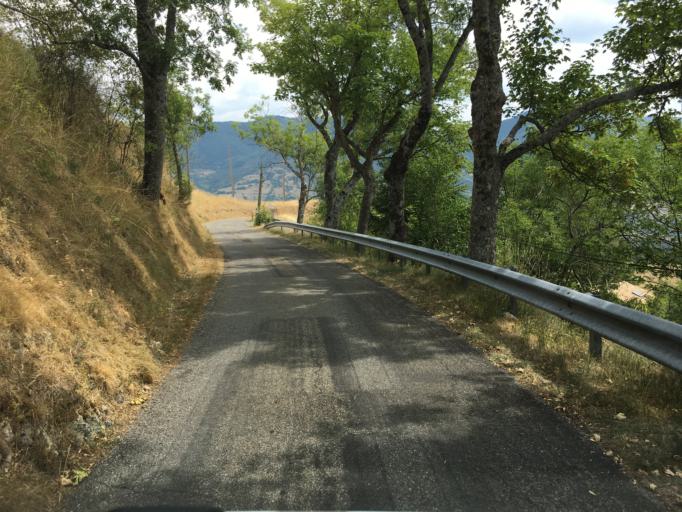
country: FR
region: Provence-Alpes-Cote d'Azur
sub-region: Departement des Alpes-de-Haute-Provence
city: Digne-les-Bains
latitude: 44.1972
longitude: 6.1356
